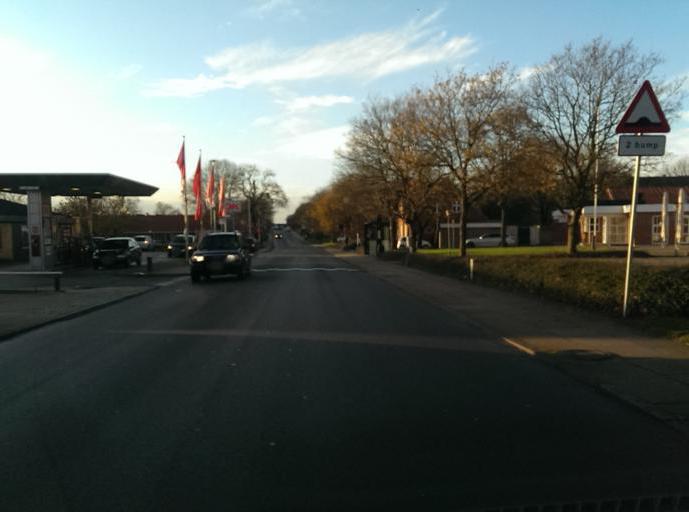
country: DK
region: South Denmark
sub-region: Esbjerg Kommune
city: Tjaereborg
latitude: 55.4632
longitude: 8.5854
